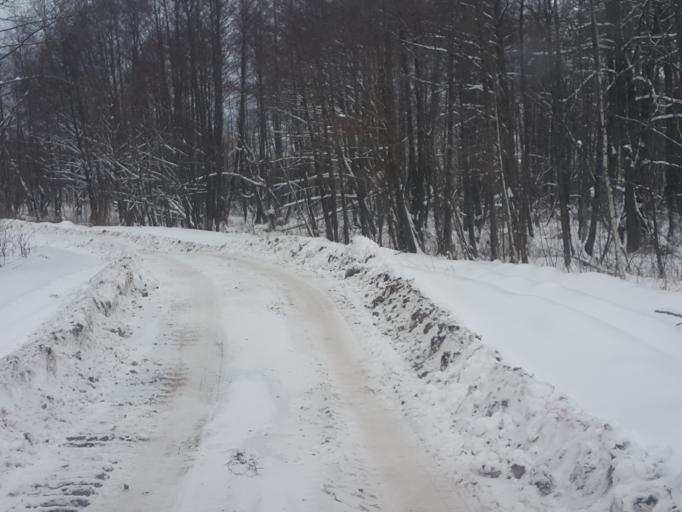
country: RU
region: Tambov
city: Platonovka
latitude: 52.8931
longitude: 41.8456
